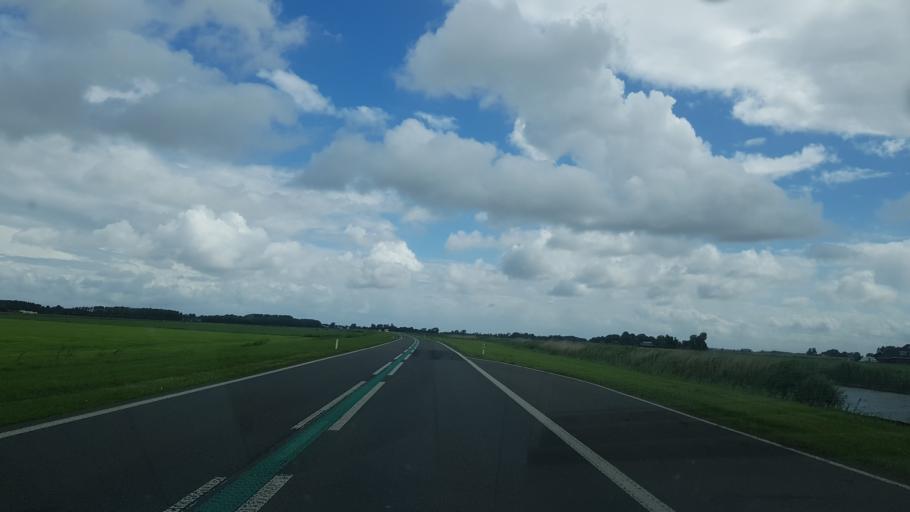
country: NL
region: Friesland
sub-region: Gemeente Dantumadiel
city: Walterswald
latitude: 53.3444
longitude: 6.0543
